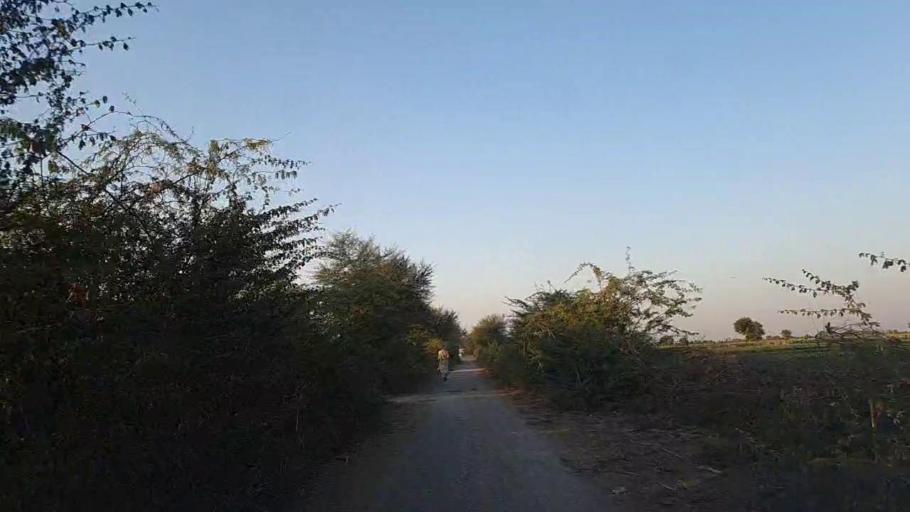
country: PK
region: Sindh
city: Naukot
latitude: 25.0335
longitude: 69.4168
